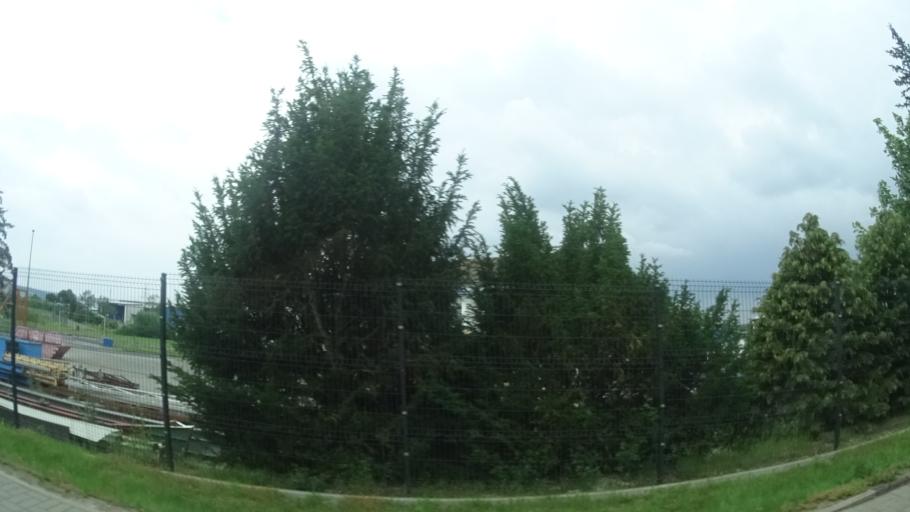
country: DE
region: Hesse
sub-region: Regierungsbezirk Kassel
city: Grossenluder
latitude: 50.5619
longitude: 9.6021
